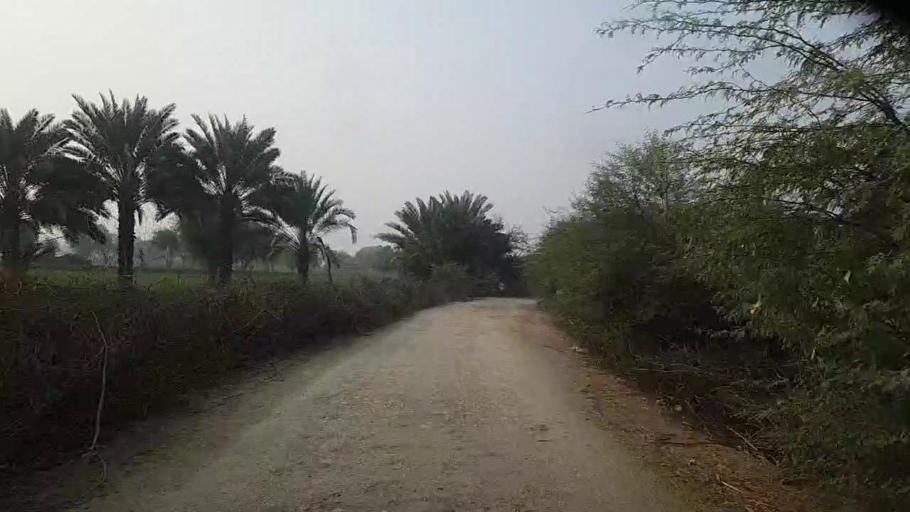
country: PK
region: Sindh
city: Bozdar
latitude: 27.1670
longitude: 68.6611
